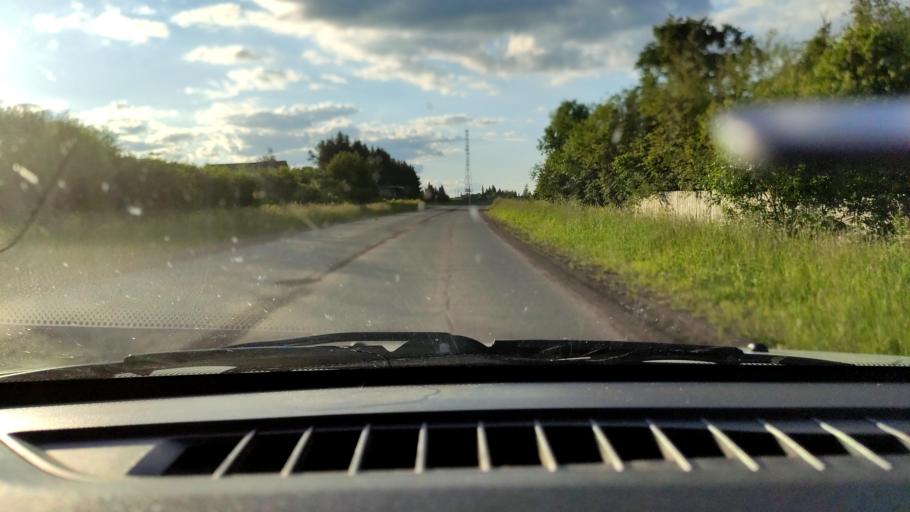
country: RU
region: Perm
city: Uinskoye
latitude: 57.1058
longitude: 56.5340
